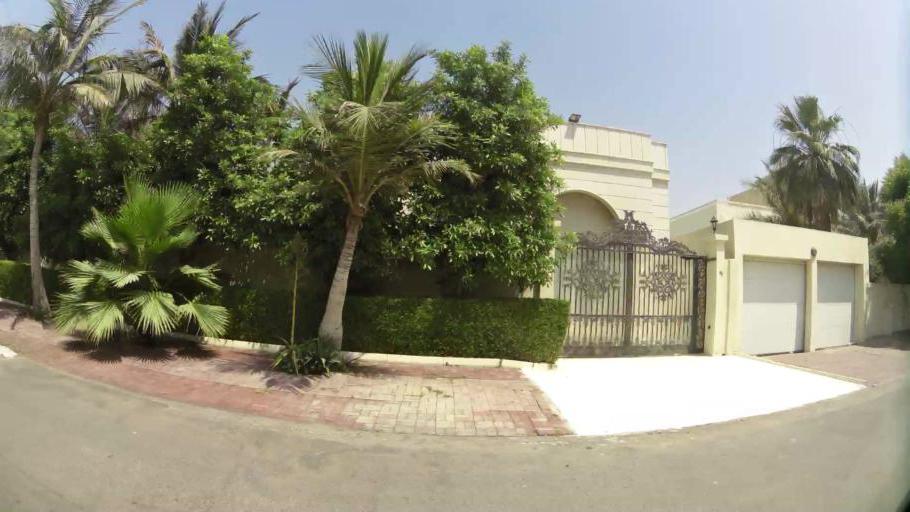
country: AE
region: Ajman
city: Ajman
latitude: 25.3976
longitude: 55.4267
